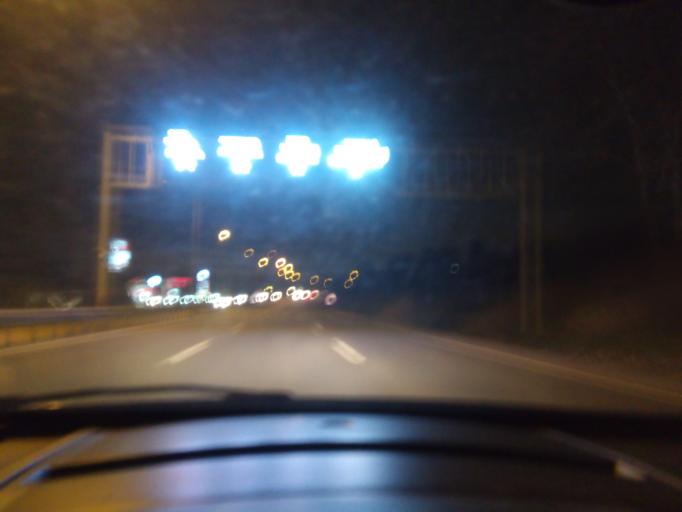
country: TR
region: Bursa
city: Niluefer
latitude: 40.3059
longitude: 28.9380
